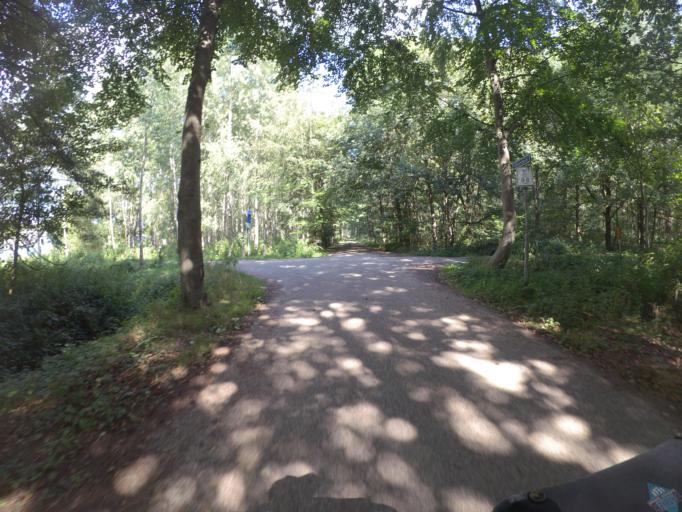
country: NL
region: North Brabant
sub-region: Gemeente Veghel
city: Eerde
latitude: 51.6255
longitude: 5.4839
